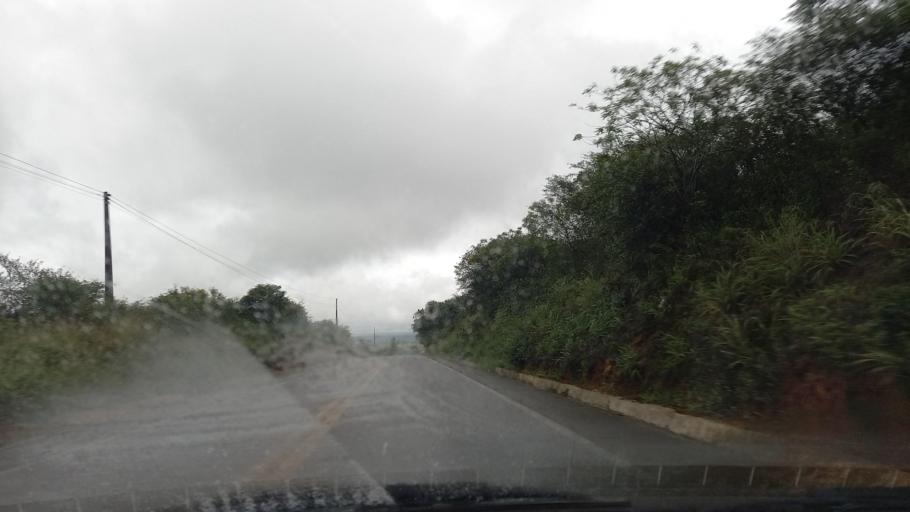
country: BR
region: Pernambuco
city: Garanhuns
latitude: -8.8551
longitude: -36.5133
